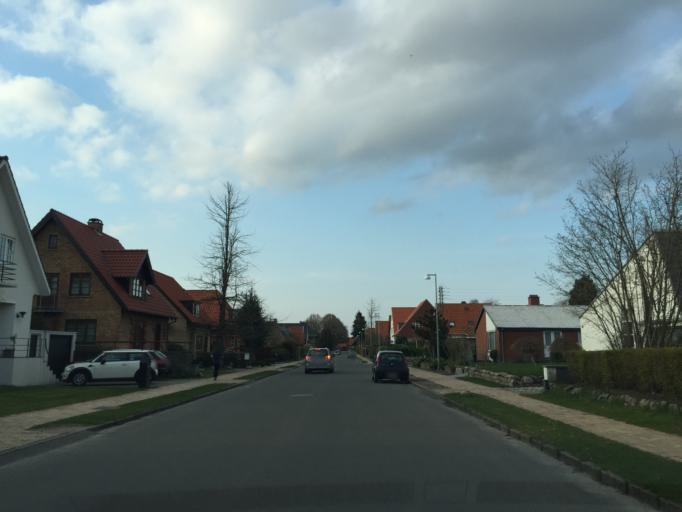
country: DK
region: South Denmark
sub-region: Odense Kommune
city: Odense
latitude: 55.3735
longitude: 10.3855
